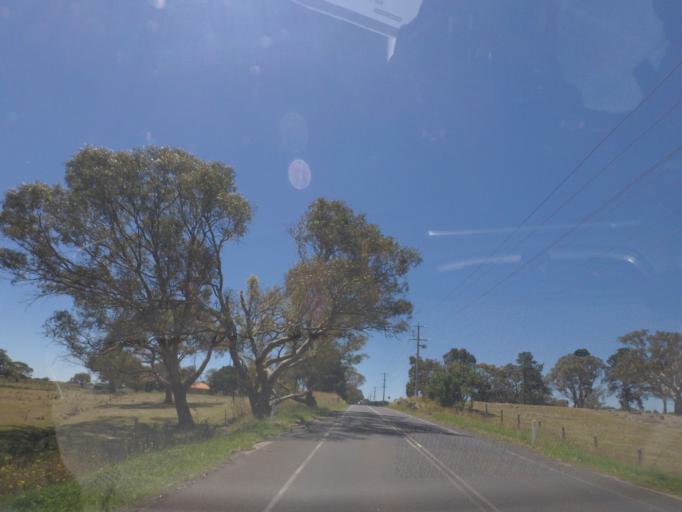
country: AU
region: Victoria
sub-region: Whittlesea
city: Mernda
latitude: -37.5410
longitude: 145.0297
